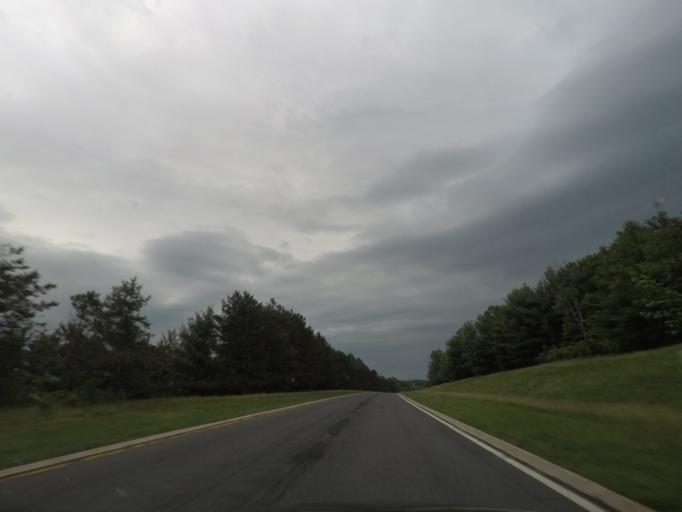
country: US
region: New York
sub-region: Columbia County
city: Philmont
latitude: 42.2733
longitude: -73.6125
